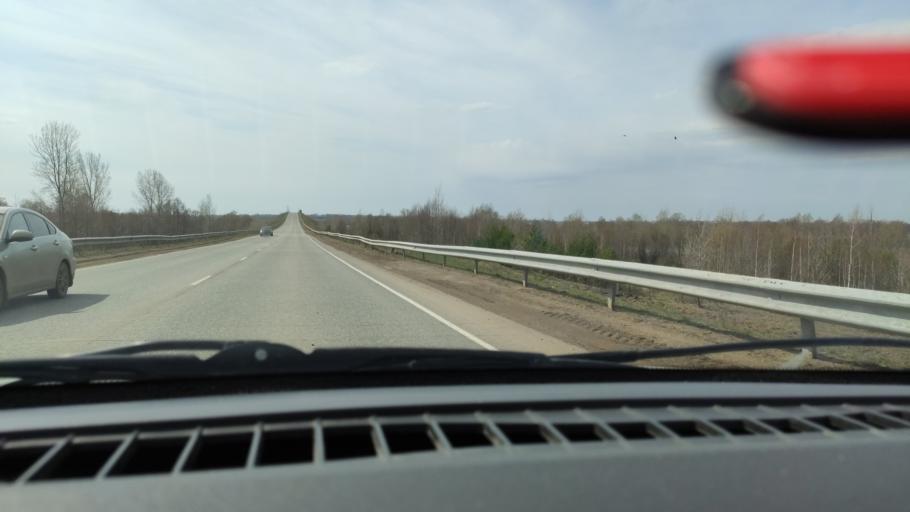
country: RU
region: Bashkortostan
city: Dyurtyuli
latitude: 55.5343
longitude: 54.8543
